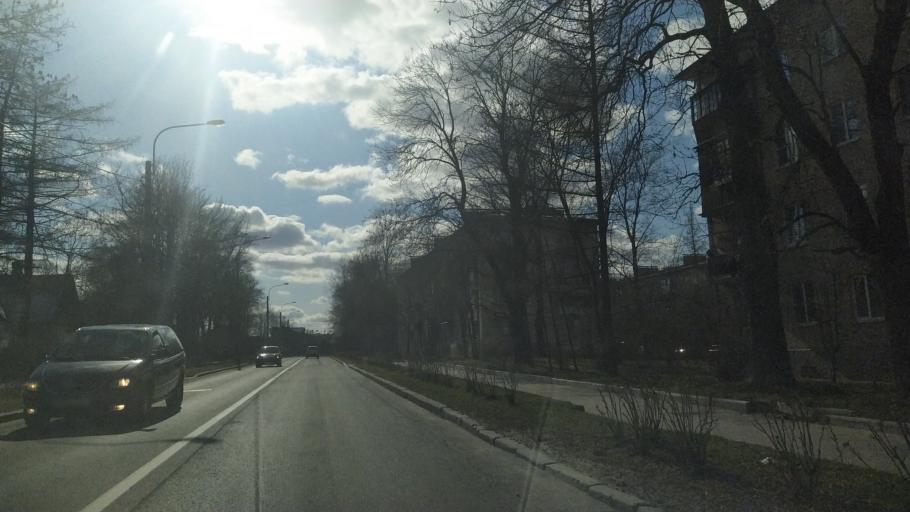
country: RU
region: St.-Petersburg
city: Pushkin
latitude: 59.7035
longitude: 30.4184
